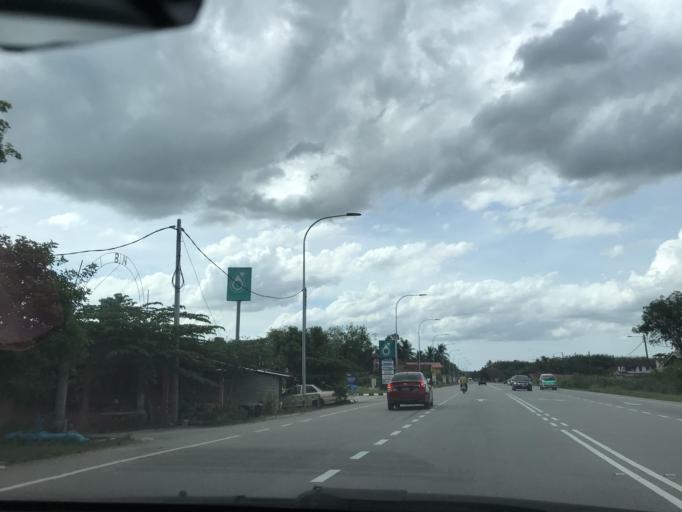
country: MY
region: Kelantan
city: Kampong Pangkal Kalong
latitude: 5.9483
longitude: 102.1920
